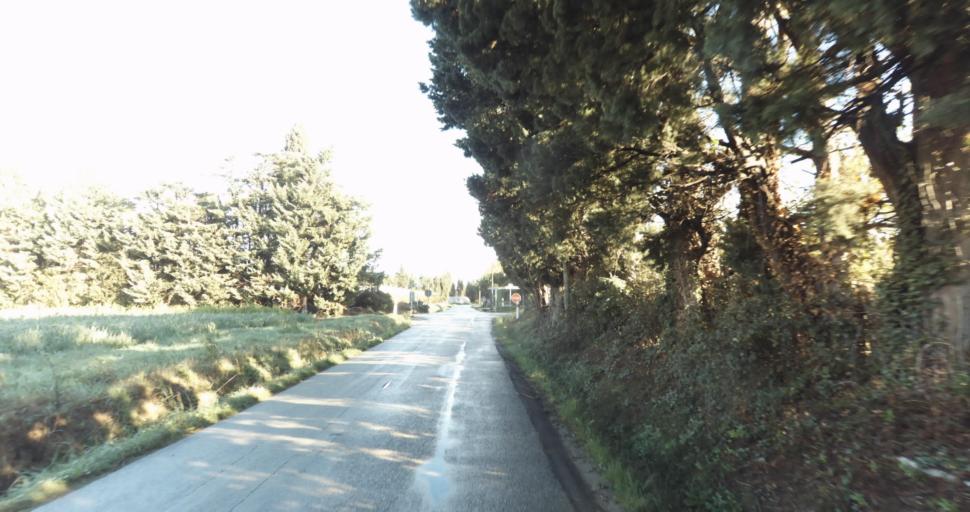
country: FR
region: Provence-Alpes-Cote d'Azur
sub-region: Departement des Bouches-du-Rhone
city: Rognonas
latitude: 43.8920
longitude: 4.7971
